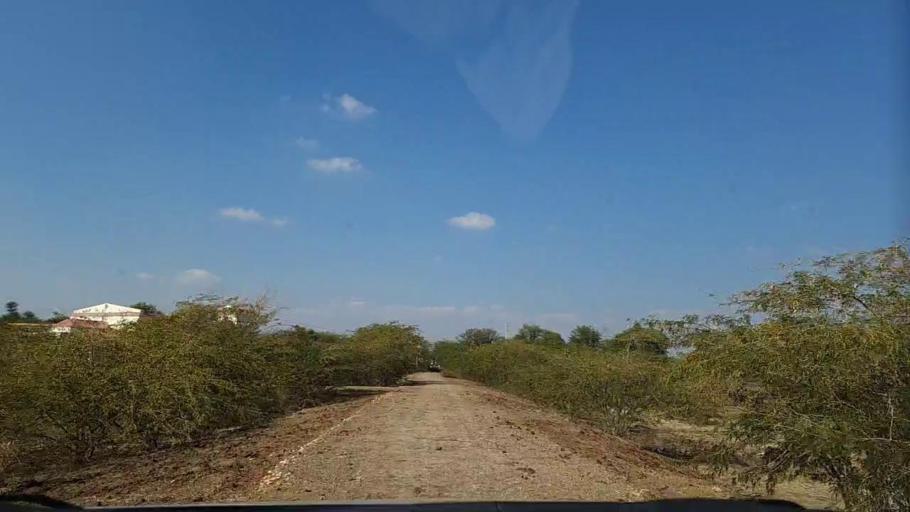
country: PK
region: Sindh
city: Pithoro
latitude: 25.6159
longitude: 69.3648
